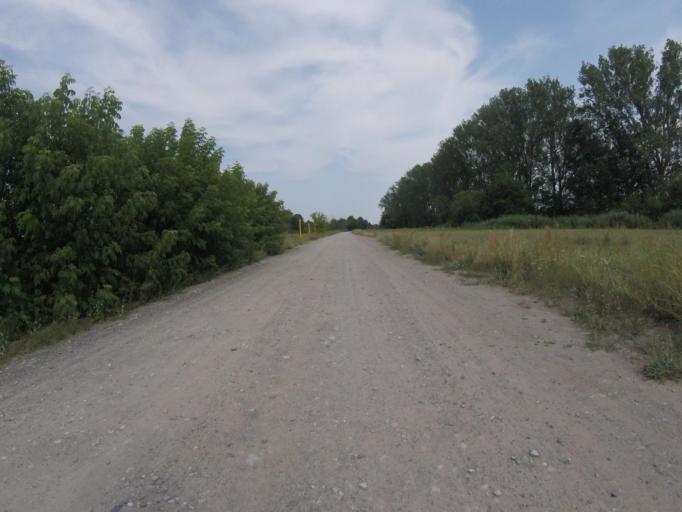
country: DE
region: Brandenburg
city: Erkner
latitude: 52.3050
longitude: 13.7765
